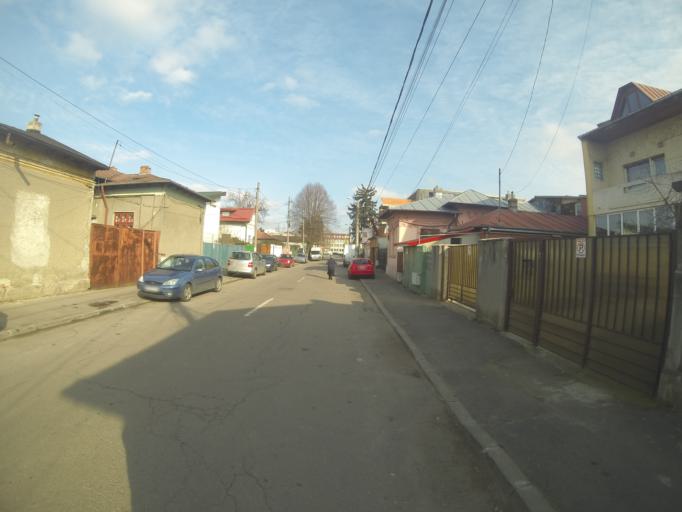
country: RO
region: Bucuresti
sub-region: Municipiul Bucuresti
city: Bucuresti
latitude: 44.4069
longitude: 26.0890
